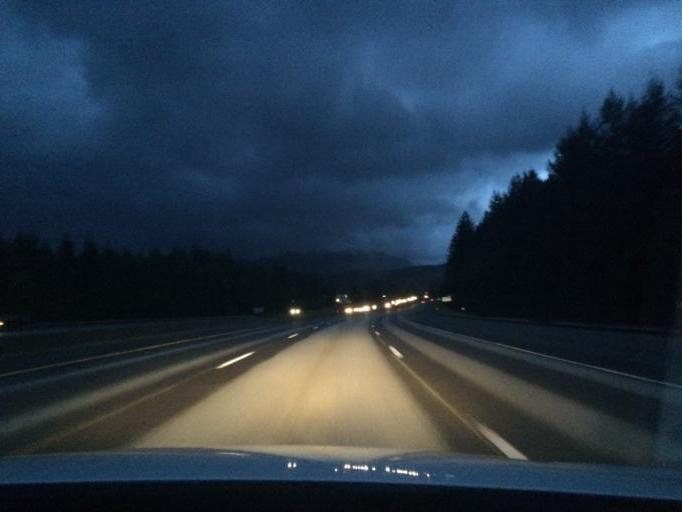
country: US
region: Washington
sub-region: King County
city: Tanner
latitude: 47.4730
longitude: -121.7413
